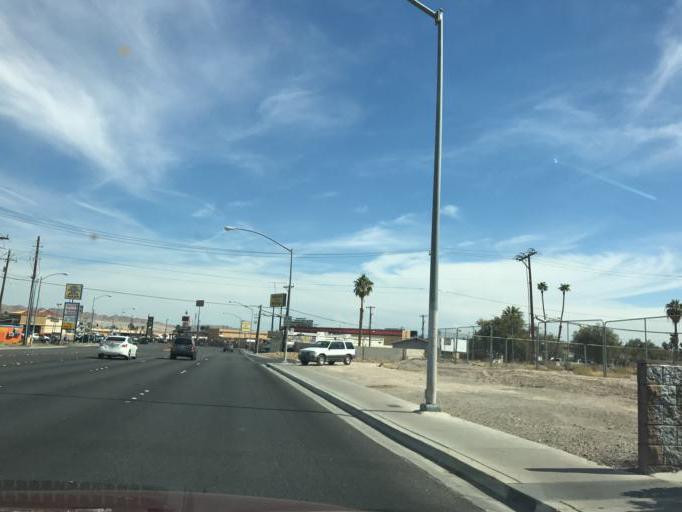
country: US
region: Nevada
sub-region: Clark County
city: Winchester
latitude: 36.1295
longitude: -115.0871
